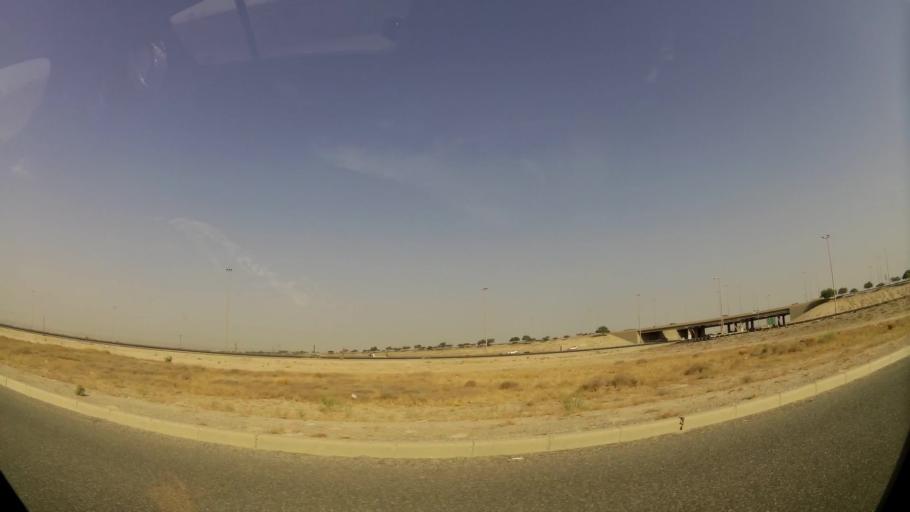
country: KW
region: Al Farwaniyah
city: Janub as Surrah
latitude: 29.1773
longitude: 47.9916
